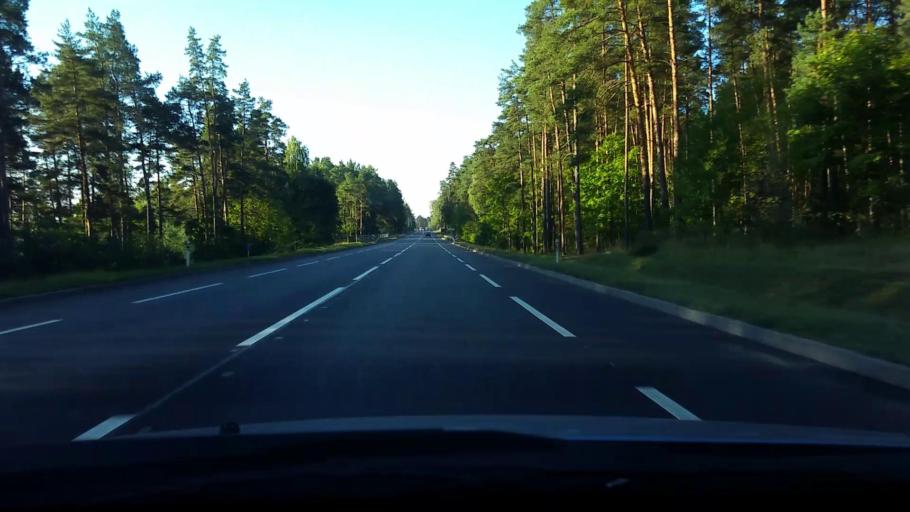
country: LV
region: Adazi
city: Adazi
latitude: 57.0509
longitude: 24.3186
